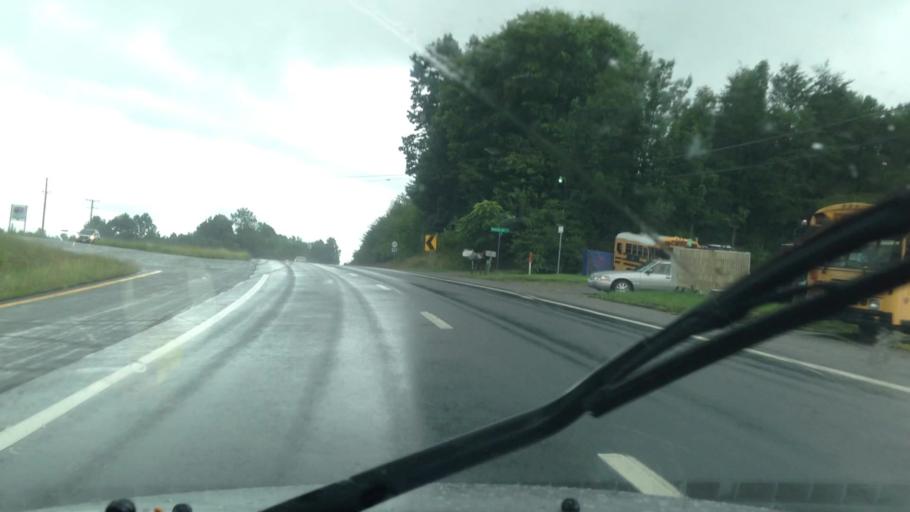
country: US
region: Virginia
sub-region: Henry County
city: Stanleytown
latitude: 36.7982
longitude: -79.9373
